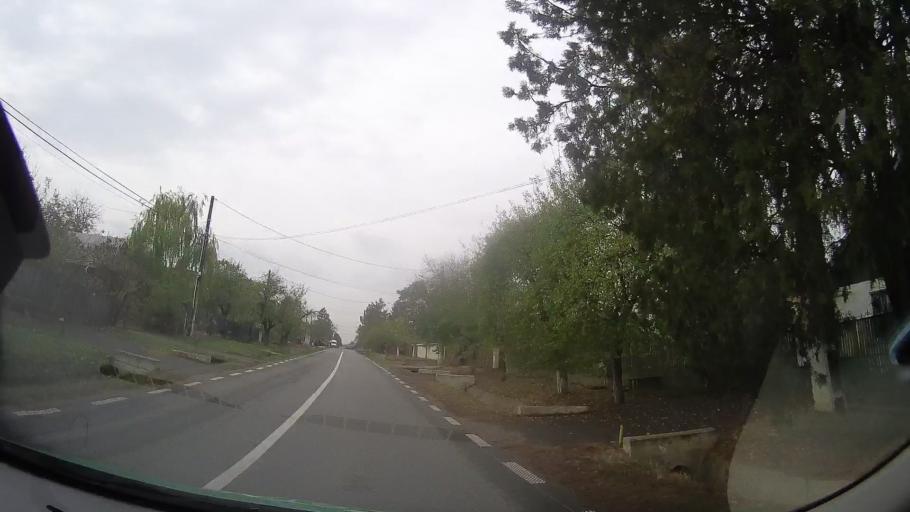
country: RO
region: Ilfov
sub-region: Comuna Gruiu
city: Gruiu
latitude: 44.7252
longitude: 26.2334
